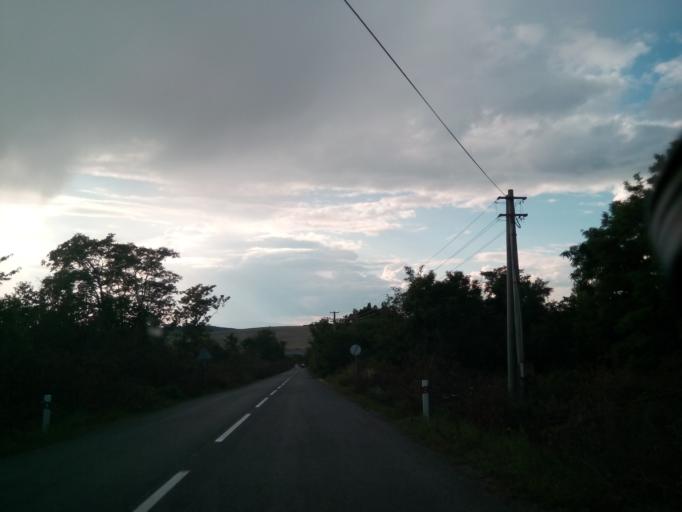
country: SK
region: Kosicky
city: Kosice
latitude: 48.6486
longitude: 21.4105
